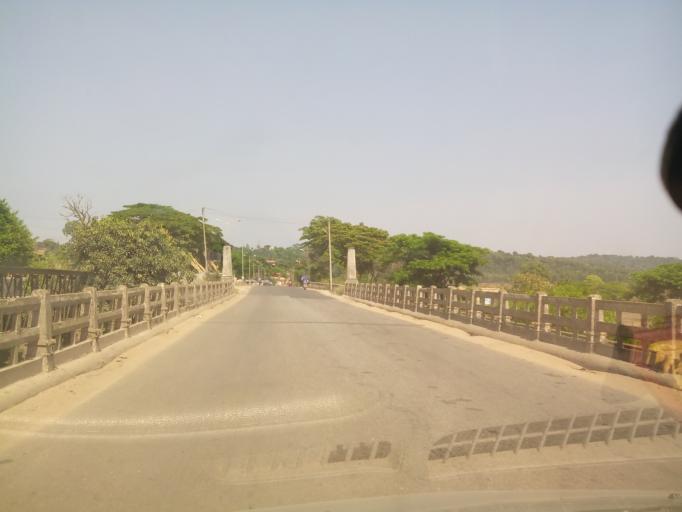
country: IN
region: Karnataka
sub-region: Hassan
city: Sakleshpur
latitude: 12.9446
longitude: 75.7936
